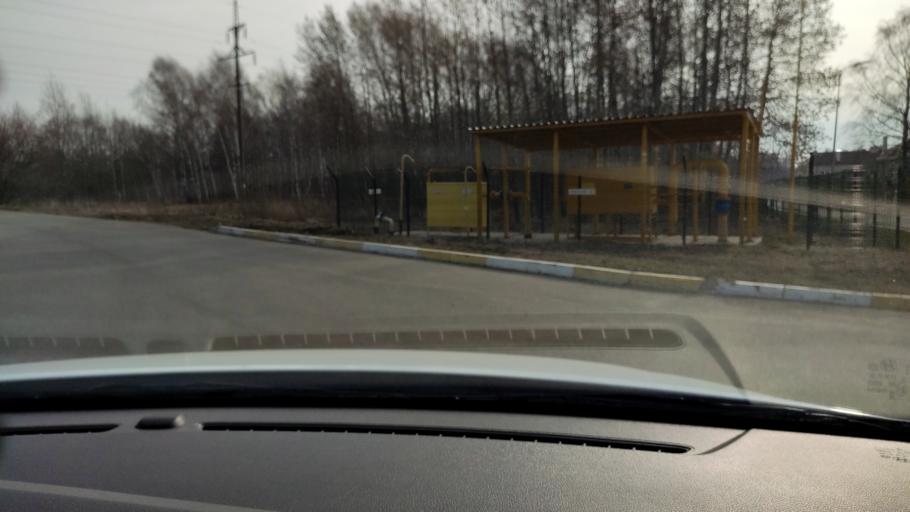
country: RU
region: Tatarstan
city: Stolbishchi
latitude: 55.7148
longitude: 49.2156
